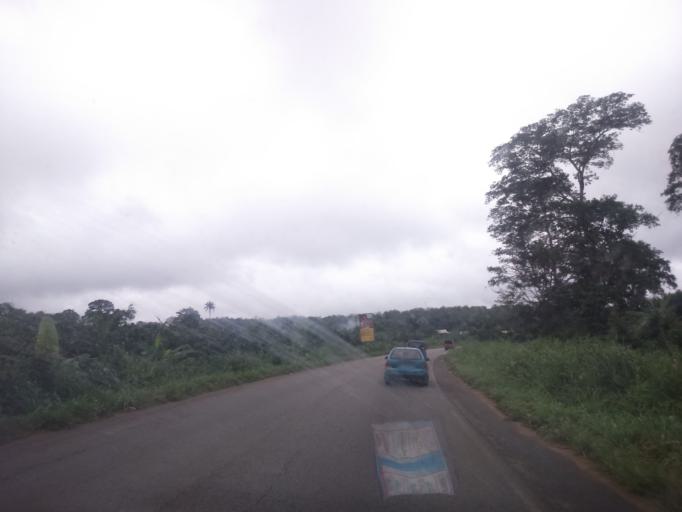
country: CI
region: Sud-Comoe
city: Bonoua
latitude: 5.2816
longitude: -3.5318
